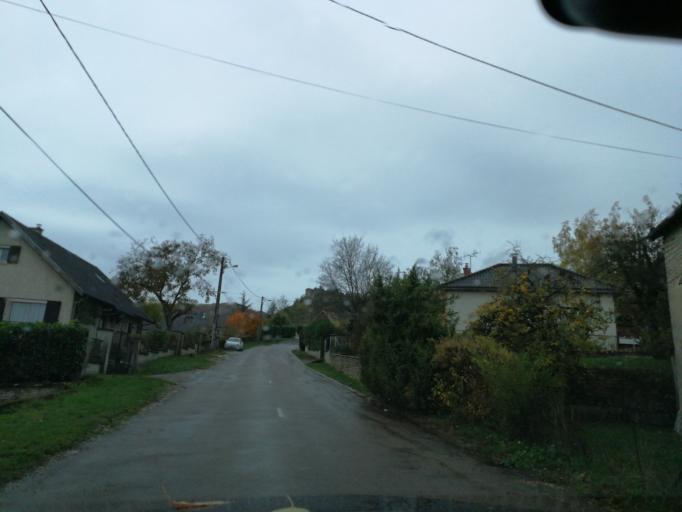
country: FR
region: Bourgogne
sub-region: Departement de la Cote-d'Or
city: Fleurey-sur-Ouche
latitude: 47.3271
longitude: 4.7972
